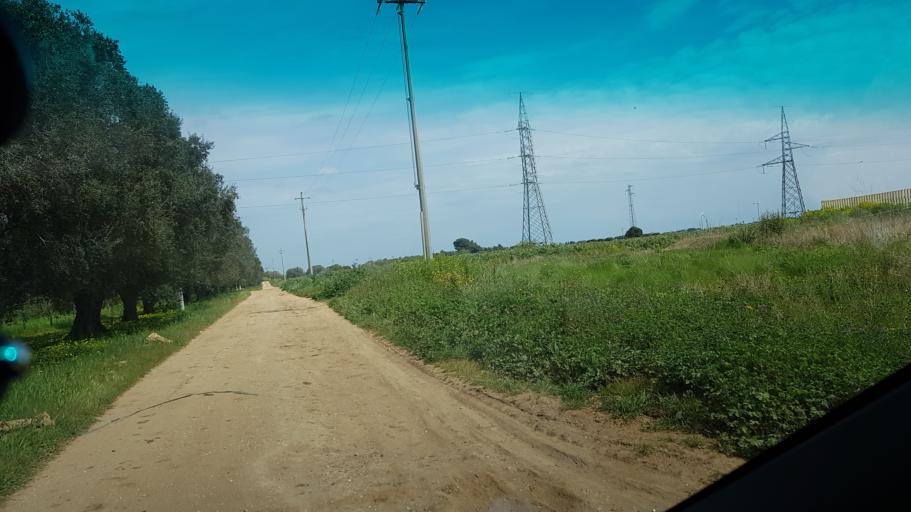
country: IT
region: Apulia
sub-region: Provincia di Brindisi
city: Mesagne
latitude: 40.6137
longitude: 17.8540
